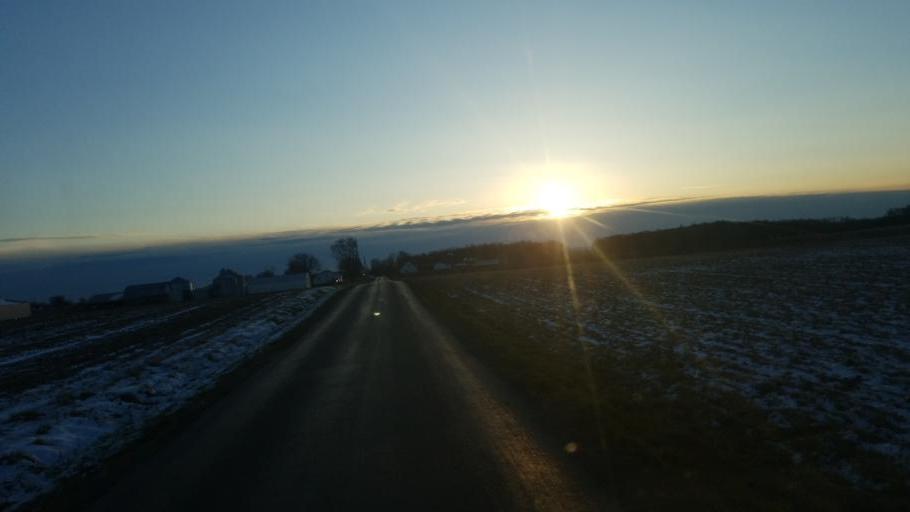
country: US
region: Ohio
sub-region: Highland County
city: Leesburg
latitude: 39.2841
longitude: -83.5135
